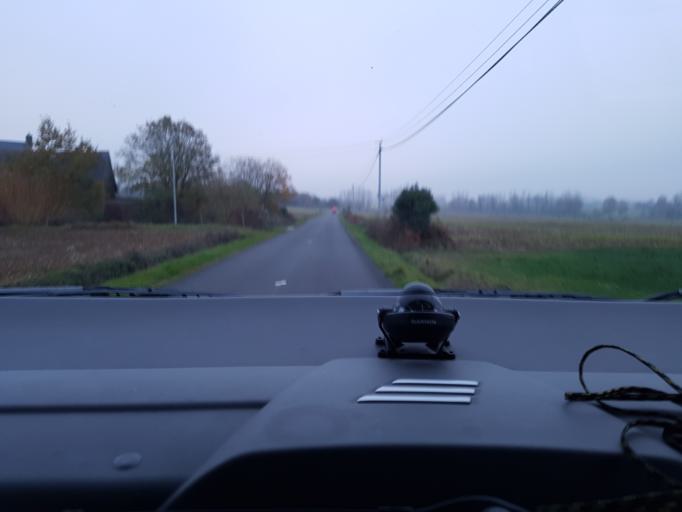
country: FR
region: Brittany
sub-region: Departement d'Ille-et-Vilaine
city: Antrain
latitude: 48.4546
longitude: -1.4193
